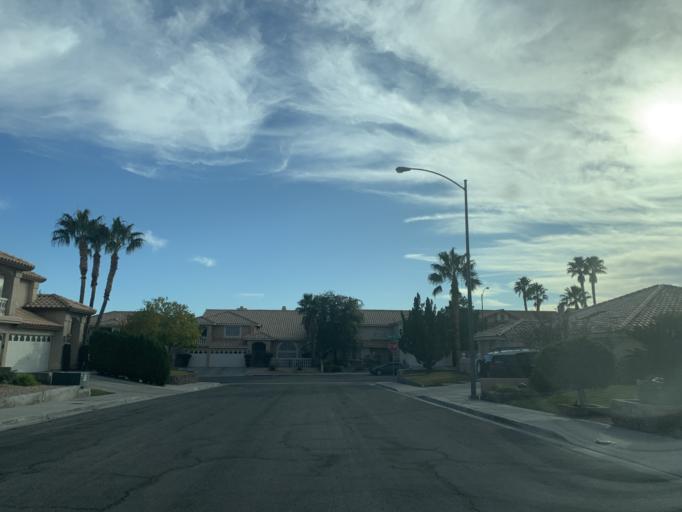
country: US
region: Nevada
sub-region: Clark County
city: Summerlin South
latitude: 36.1289
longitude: -115.3026
